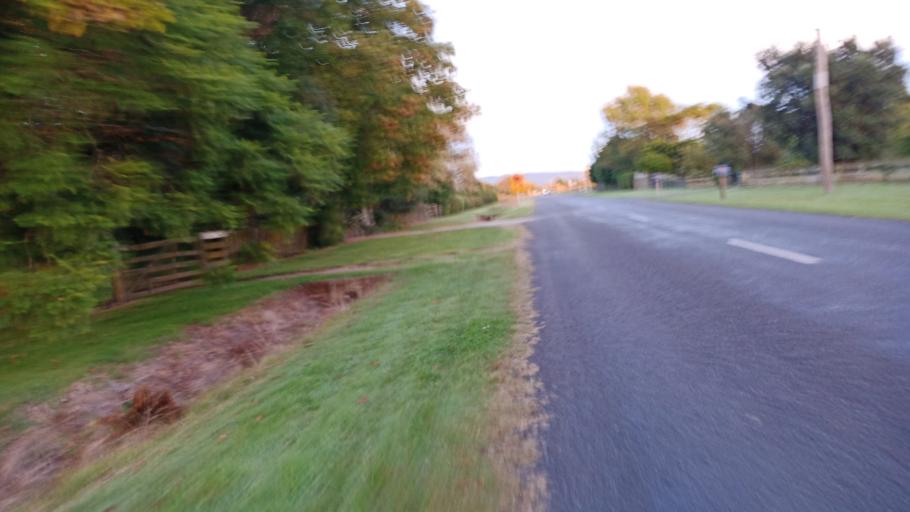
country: NZ
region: Gisborne
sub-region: Gisborne District
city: Gisborne
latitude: -38.6339
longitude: 177.9749
